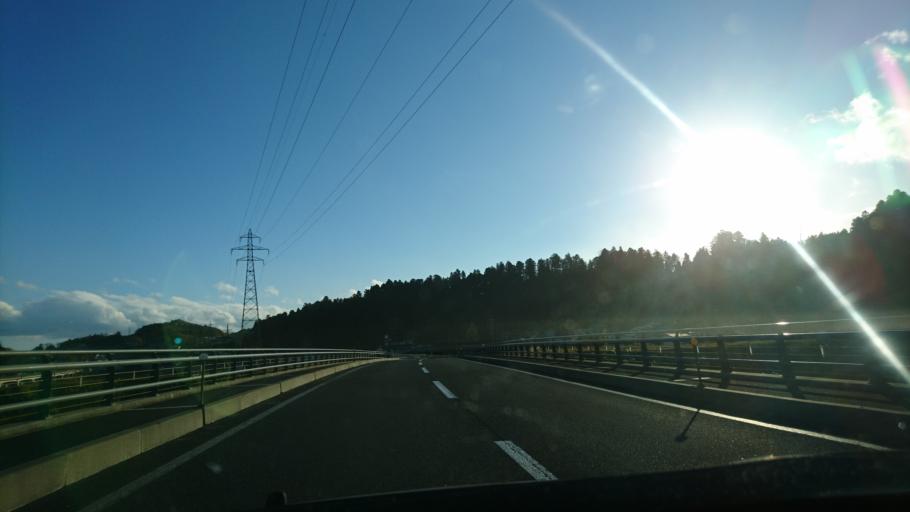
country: JP
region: Iwate
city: Ichinoseki
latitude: 39.0050
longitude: 141.1081
